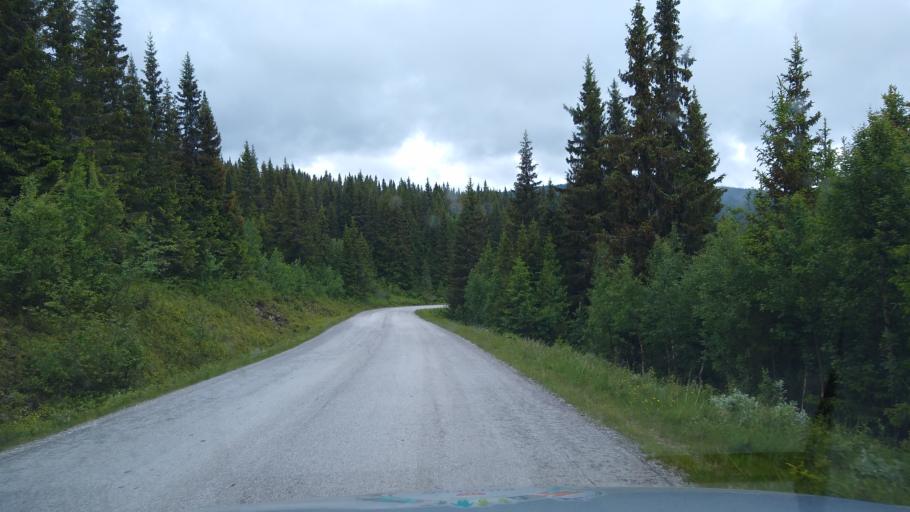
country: NO
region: Oppland
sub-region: Ringebu
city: Ringebu
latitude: 61.4843
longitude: 10.1181
